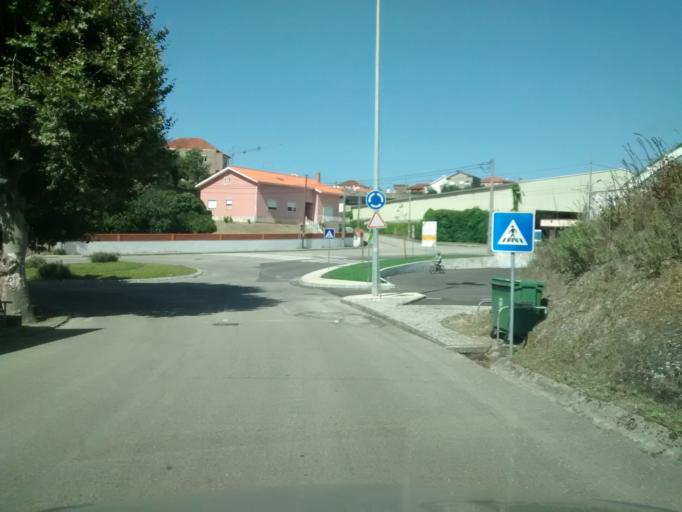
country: PT
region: Aveiro
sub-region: Mealhada
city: Pampilhosa do Botao
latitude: 40.3852
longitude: -8.3825
